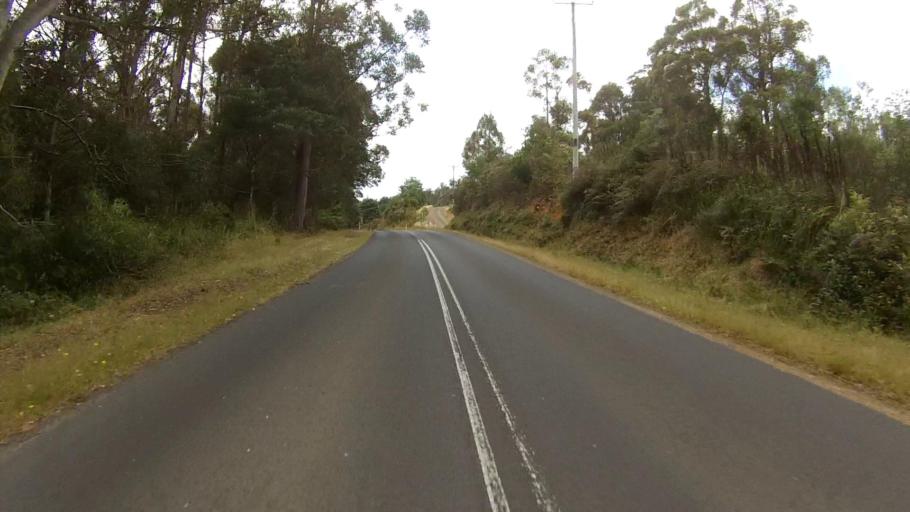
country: AU
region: Tasmania
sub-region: Huon Valley
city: Cygnet
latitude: -43.1479
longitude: 147.1528
